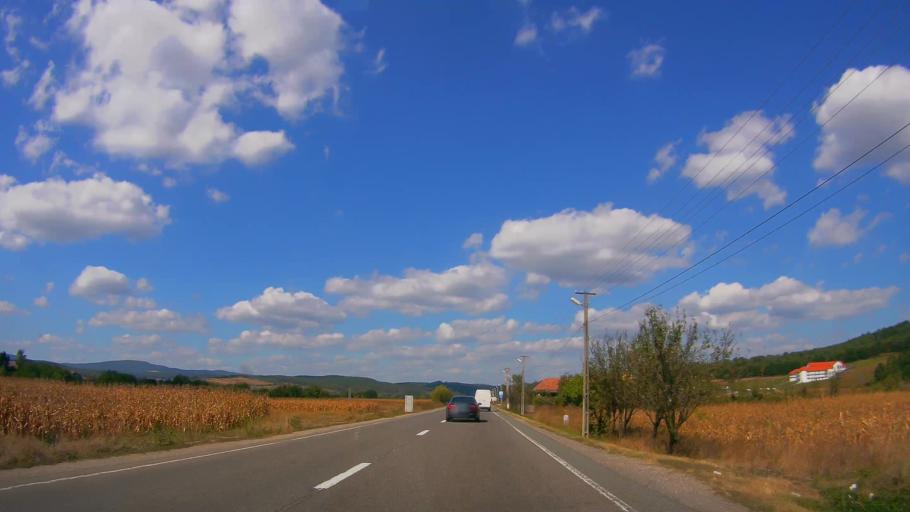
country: RO
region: Salaj
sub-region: Comuna Romanasi
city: Romanasi
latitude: 47.0961
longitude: 23.1885
